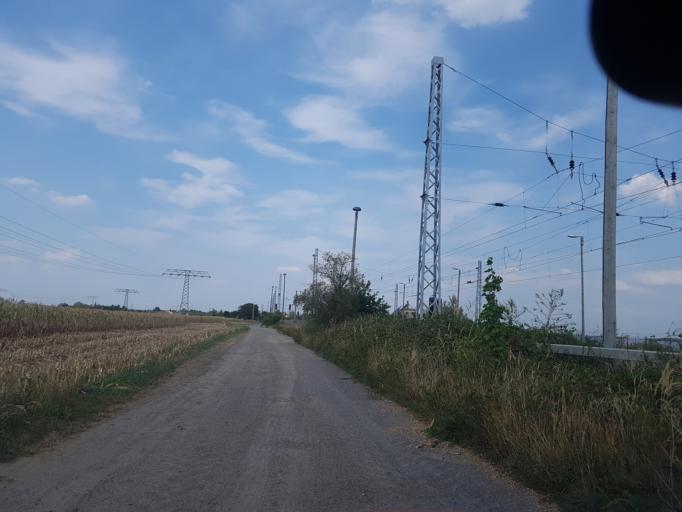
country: DE
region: Saxony
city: Wulknitz
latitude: 51.3623
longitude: 13.3812
